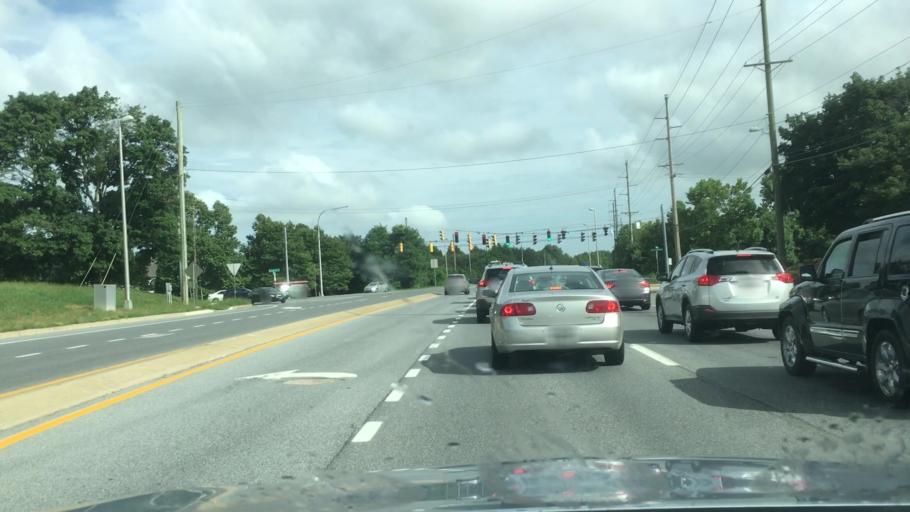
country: US
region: Delaware
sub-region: New Castle County
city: North Star
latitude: 39.7671
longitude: -75.7072
